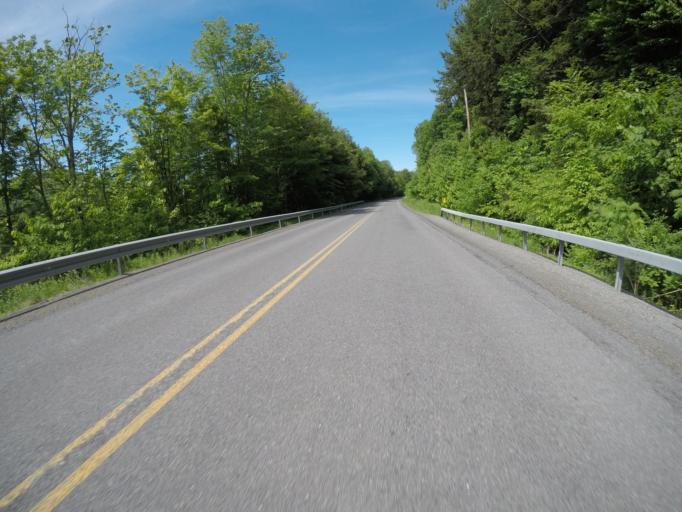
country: US
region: New York
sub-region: Delaware County
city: Delhi
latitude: 42.1018
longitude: -74.8260
